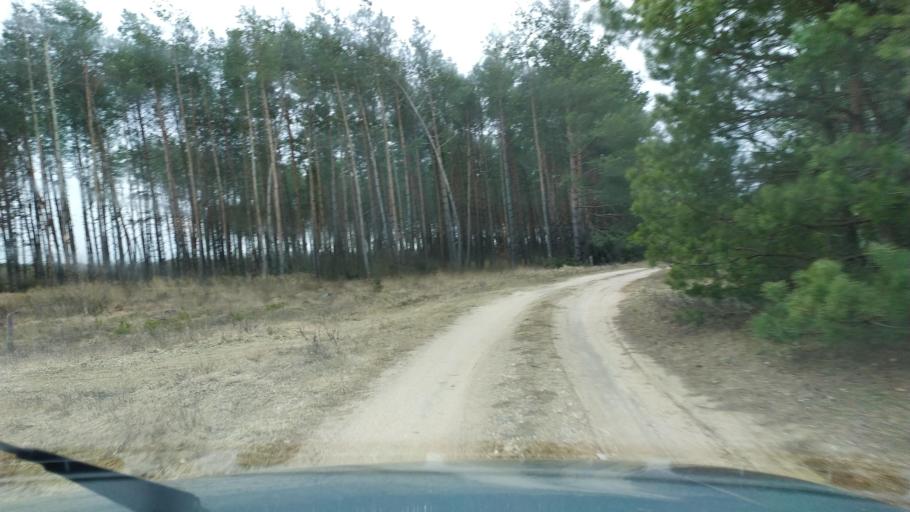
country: BY
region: Brest
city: Zhabinka
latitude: 52.4032
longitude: 24.0698
